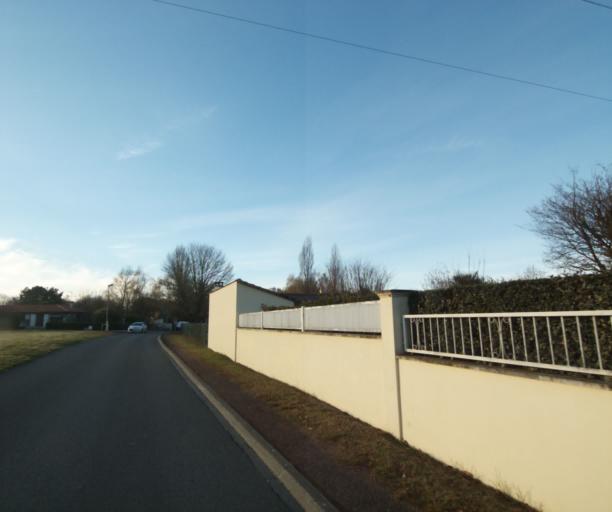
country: FR
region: Poitou-Charentes
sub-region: Departement de la Charente-Maritime
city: Fontcouverte
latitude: 45.7670
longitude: -0.5852
